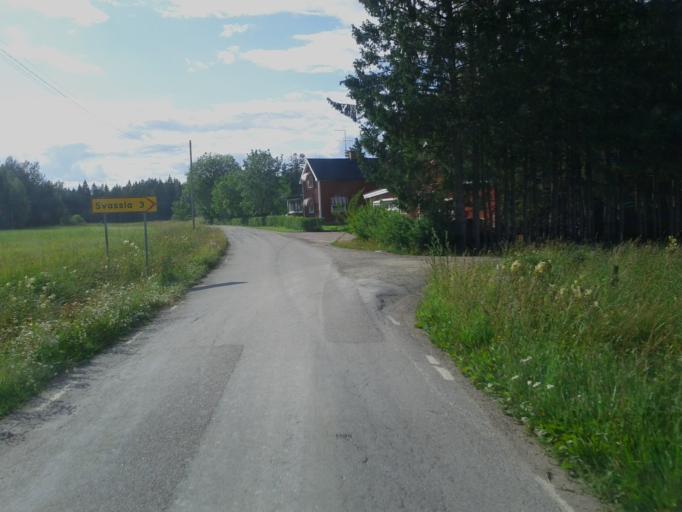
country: SE
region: Vaestmanland
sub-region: Sala Kommun
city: Sala
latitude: 59.9245
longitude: 16.4951
